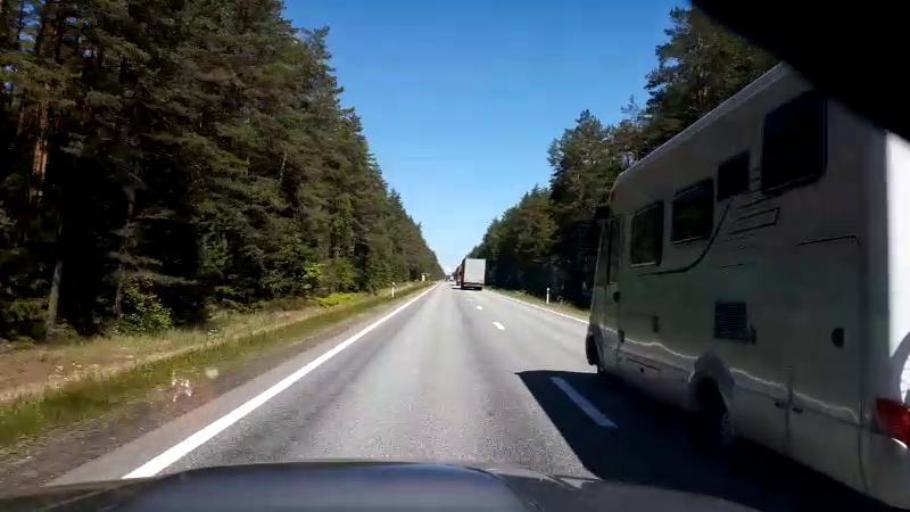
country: LV
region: Salacgrivas
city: Salacgriva
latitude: 57.5395
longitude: 24.4317
